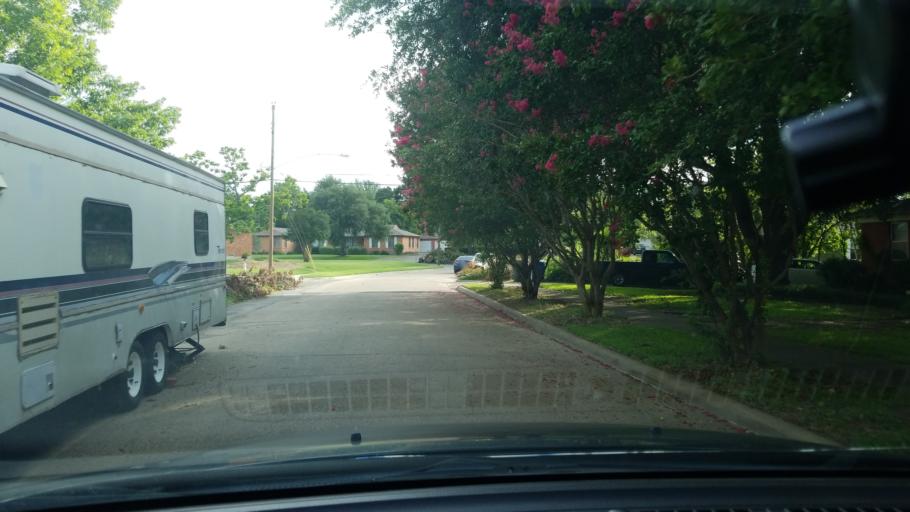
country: US
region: Texas
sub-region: Dallas County
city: Highland Park
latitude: 32.8245
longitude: -96.6921
